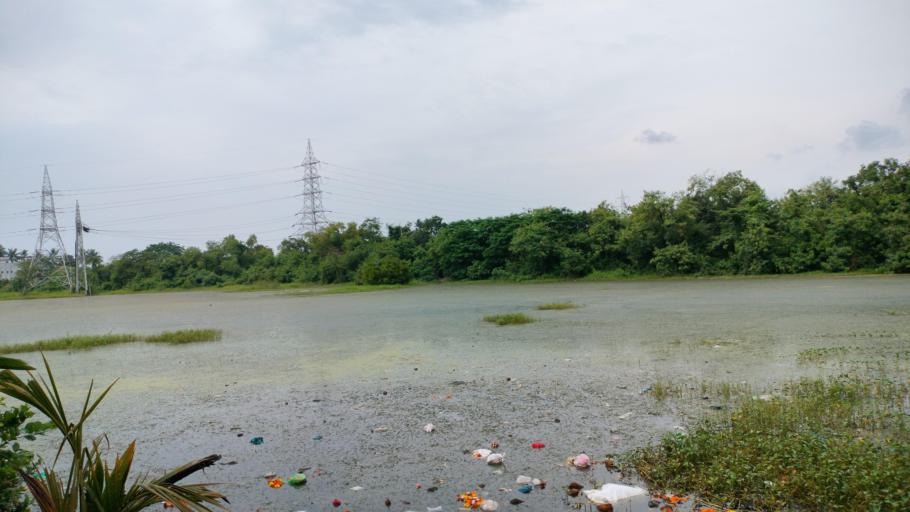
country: IN
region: Maharashtra
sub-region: Mumbai Suburban
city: Powai
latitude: 19.1440
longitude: 72.8181
